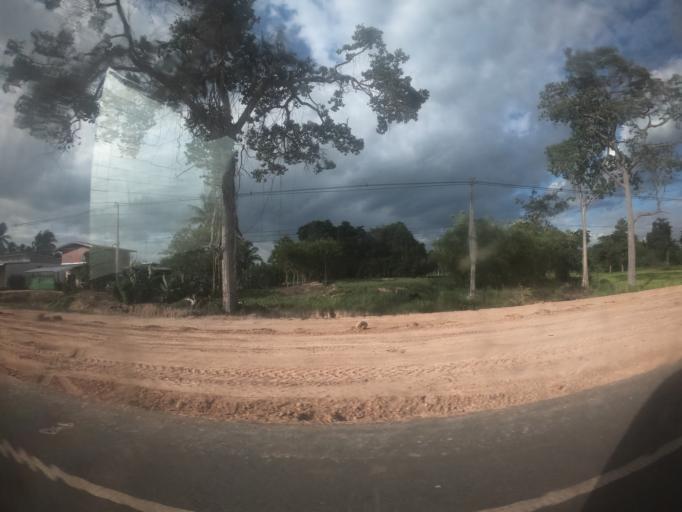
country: TH
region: Surin
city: Kap Choeng
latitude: 14.4872
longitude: 103.5778
